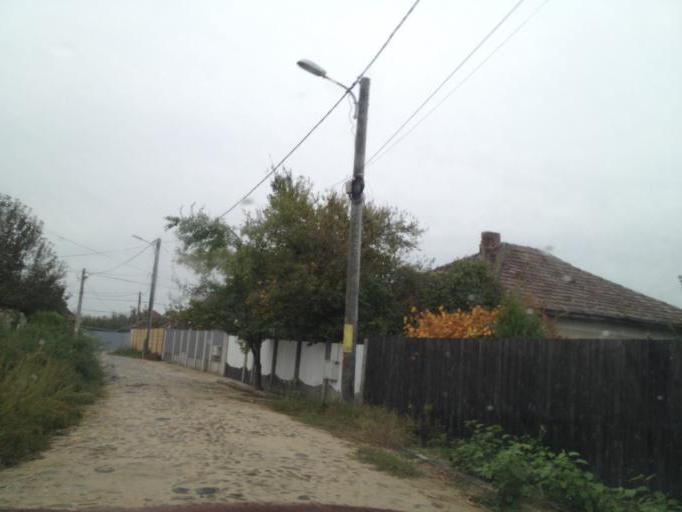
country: RO
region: Dolj
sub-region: Municipiul Craiova
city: Mofleni
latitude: 44.3122
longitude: 23.7754
